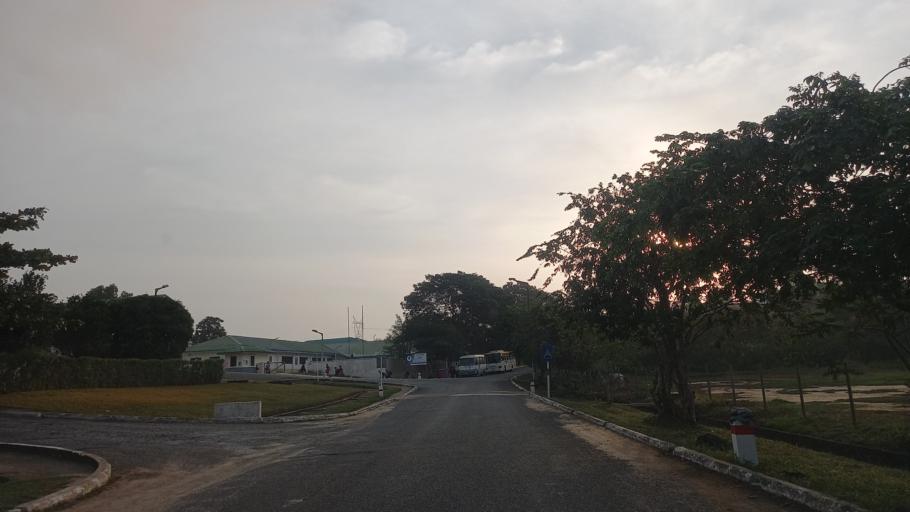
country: GH
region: Western
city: Shama Junction
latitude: 4.9796
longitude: -1.6571
